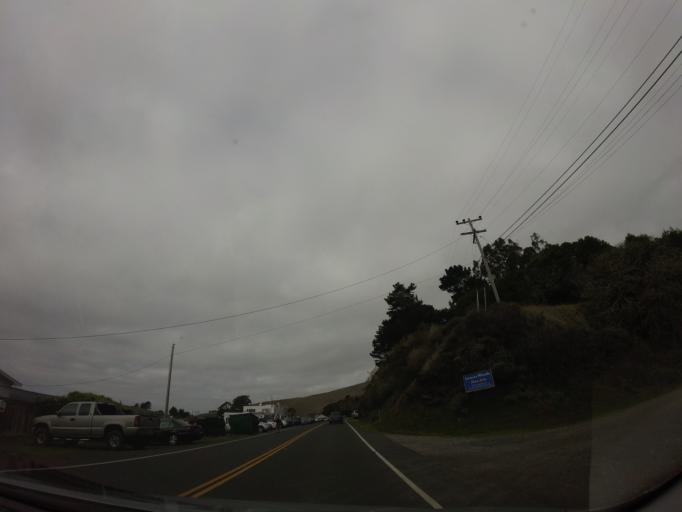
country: US
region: California
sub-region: Marin County
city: Inverness
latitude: 38.1464
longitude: -122.8826
